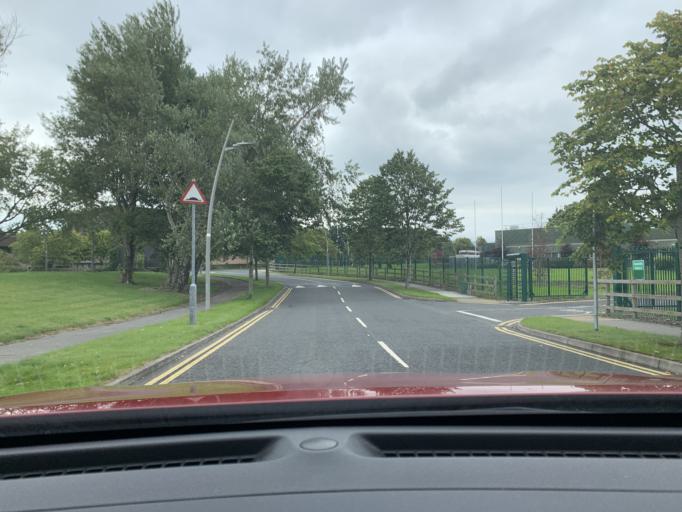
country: IE
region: Connaught
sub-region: Sligo
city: Sligo
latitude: 54.2762
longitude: -8.4964
